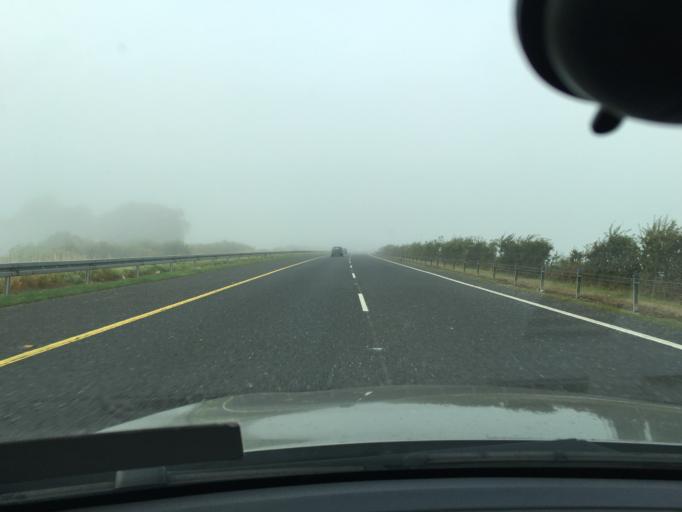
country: IE
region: Leinster
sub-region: An Mhi
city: Enfield
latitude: 53.4042
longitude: -6.8144
